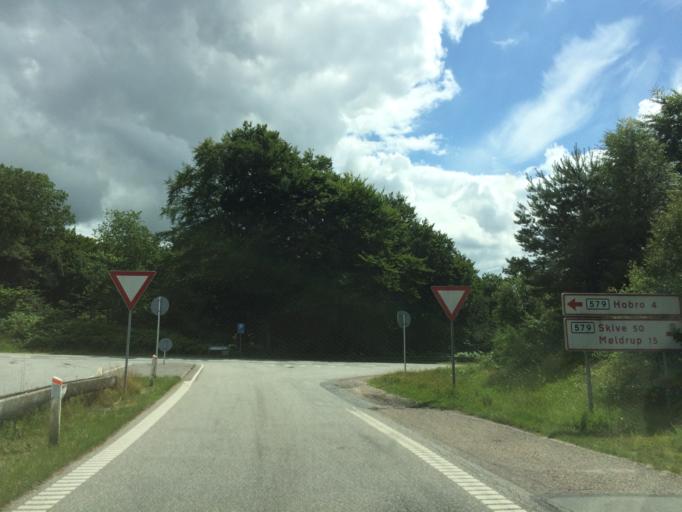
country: DK
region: North Denmark
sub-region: Mariagerfjord Kommune
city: Hobro
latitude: 56.6236
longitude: 9.7306
